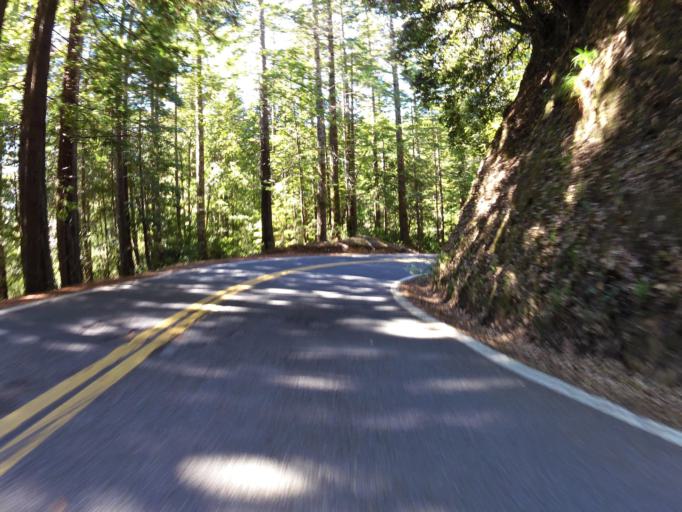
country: US
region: California
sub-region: Humboldt County
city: Redway
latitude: 39.7947
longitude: -123.8145
